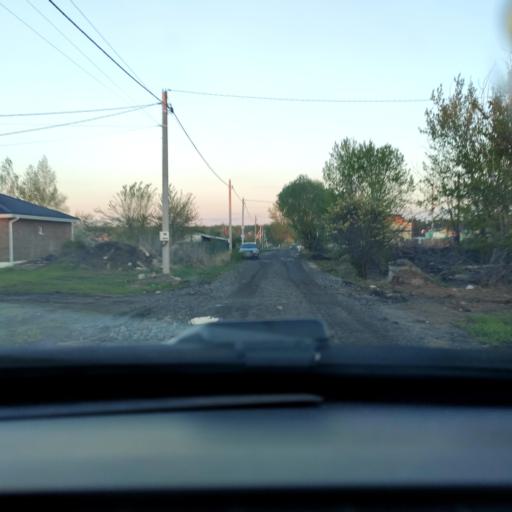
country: RU
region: Voronezj
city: Novaya Usman'
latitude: 51.6566
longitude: 39.4215
